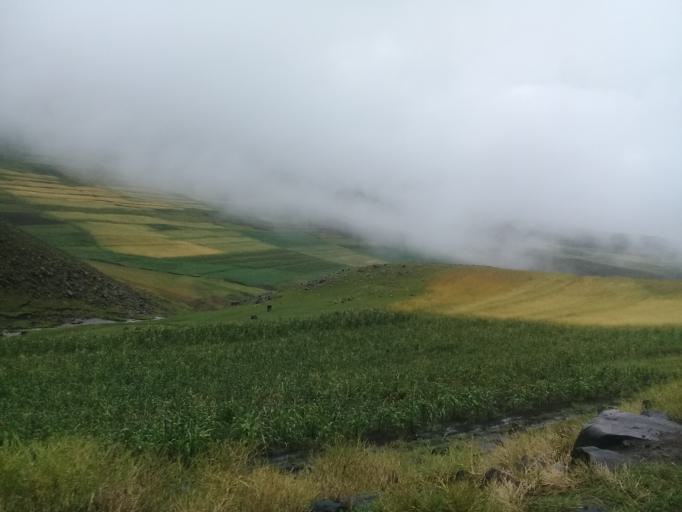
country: LS
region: Mokhotlong
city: Mokhotlong
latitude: -29.3846
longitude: 28.9800
